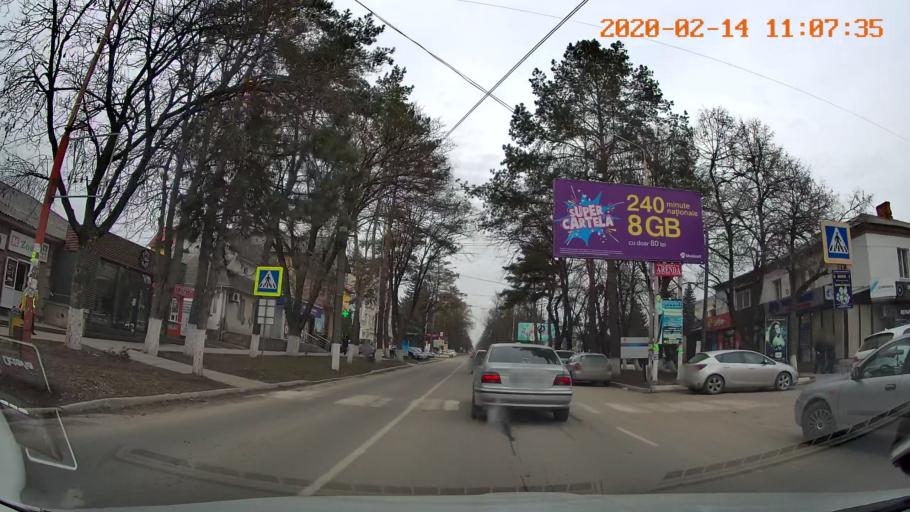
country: MD
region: Raionul Edinet
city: Edinet
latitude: 48.1698
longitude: 27.3055
